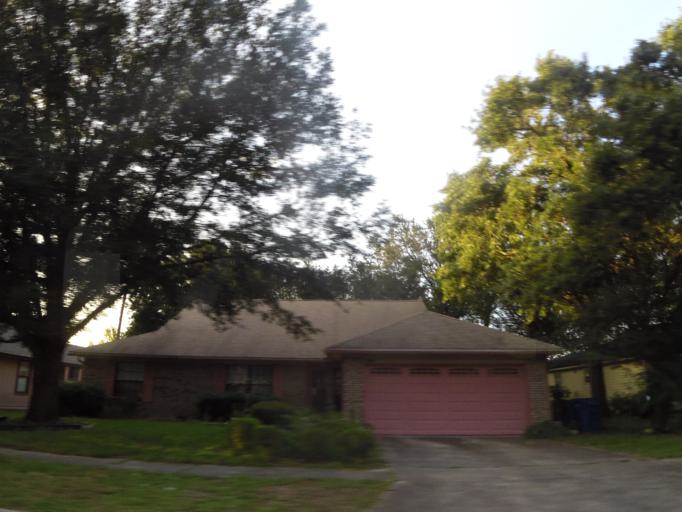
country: US
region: Florida
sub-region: Duval County
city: Atlantic Beach
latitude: 30.3612
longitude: -81.4945
